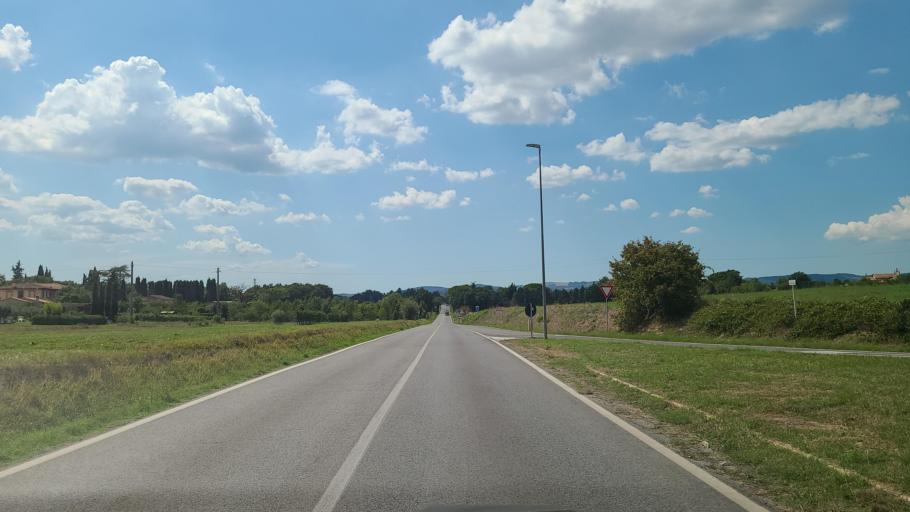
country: IT
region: Tuscany
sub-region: Provincia di Siena
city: Colle di Val d'Elsa
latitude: 43.4191
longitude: 11.0969
